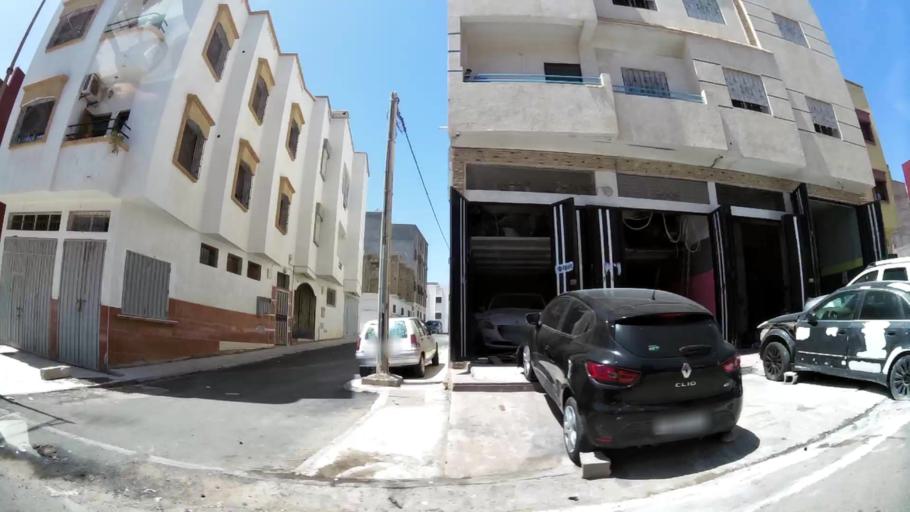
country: MA
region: Oued ed Dahab-Lagouira
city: Dakhla
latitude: 30.4314
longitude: -9.5508
